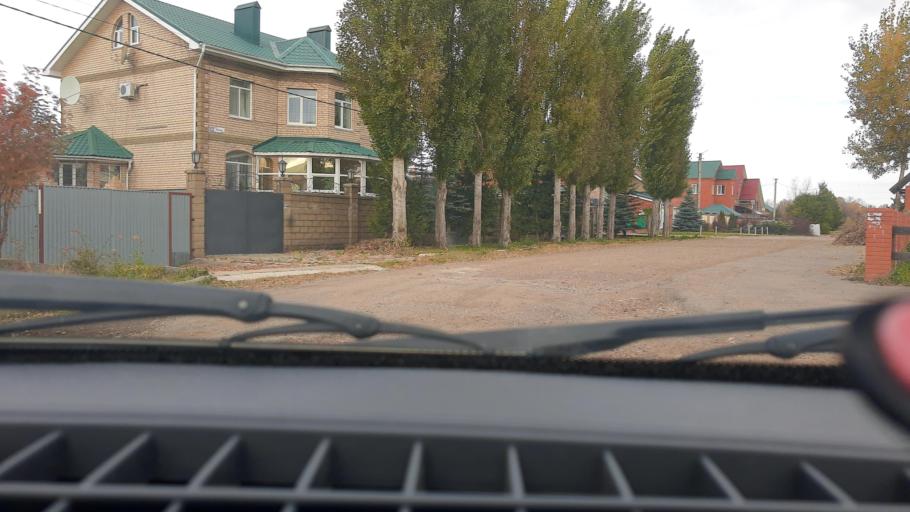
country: RU
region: Bashkortostan
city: Mikhaylovka
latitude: 54.7951
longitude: 55.9437
